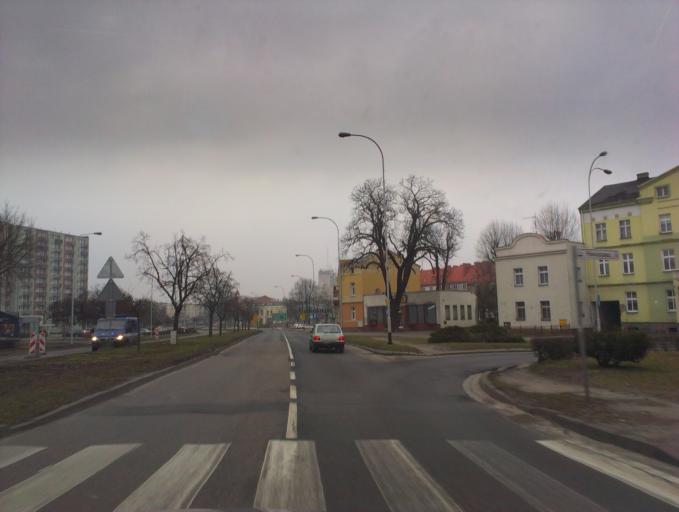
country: PL
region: Greater Poland Voivodeship
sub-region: Powiat pilski
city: Pila
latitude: 53.1450
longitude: 16.7397
